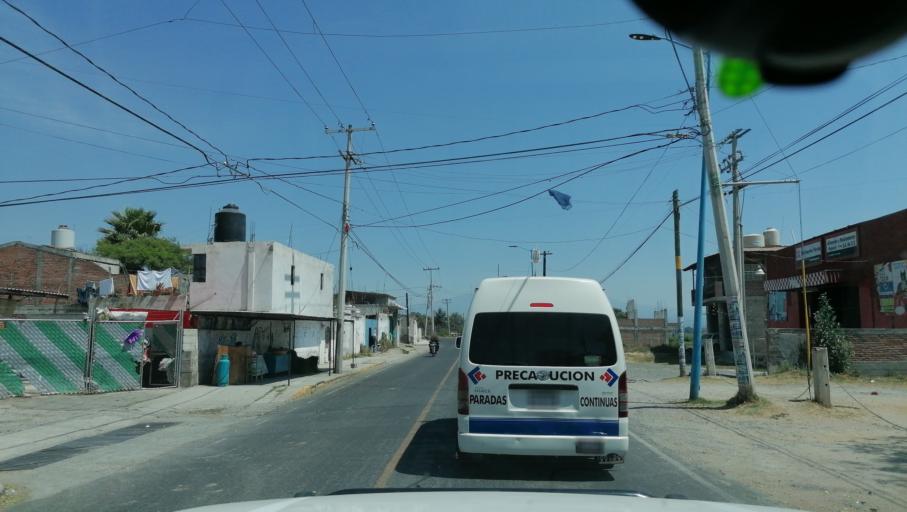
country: MX
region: Tlaxcala
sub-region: Tetlatlahuca
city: Tetlatlahuca
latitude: 19.2315
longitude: -98.2910
